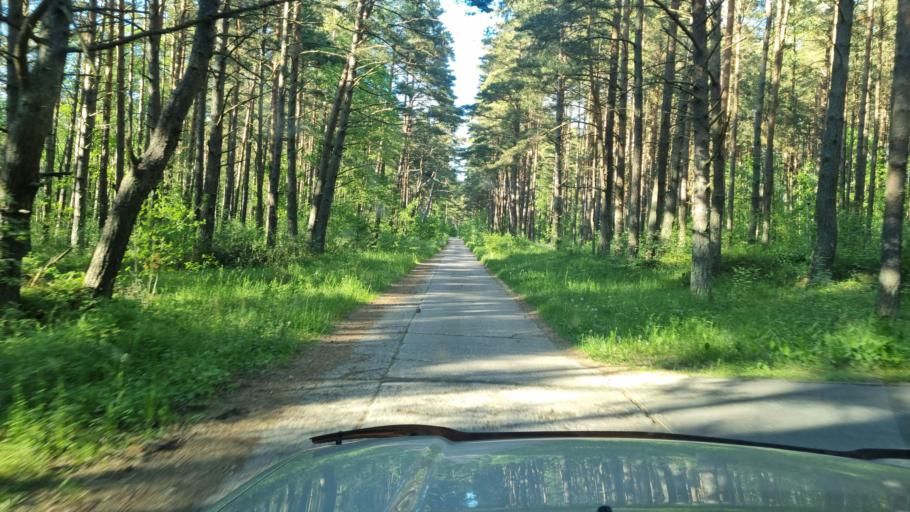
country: LV
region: Ventspils
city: Ventspils
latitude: 57.3751
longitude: 21.5269
